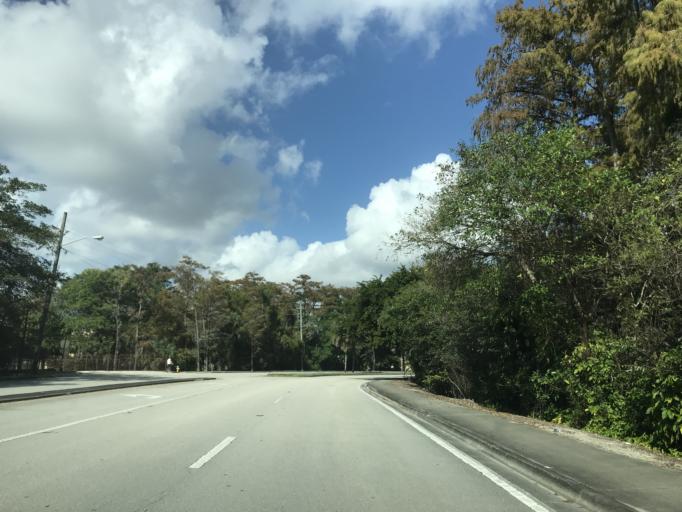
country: US
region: Florida
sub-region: Broward County
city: Margate
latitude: 26.2699
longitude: -80.1992
